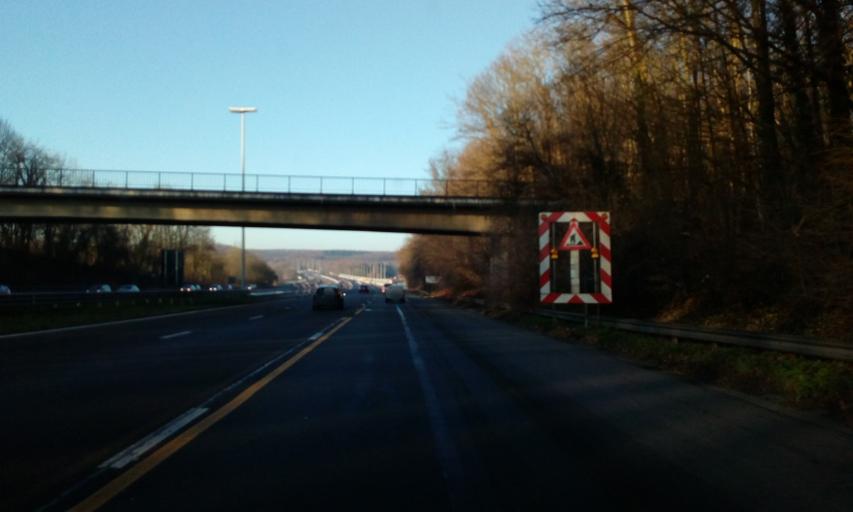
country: BE
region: Wallonia
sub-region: Province du Brabant Wallon
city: Braine-le-Chateau
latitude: 50.6792
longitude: 4.3086
